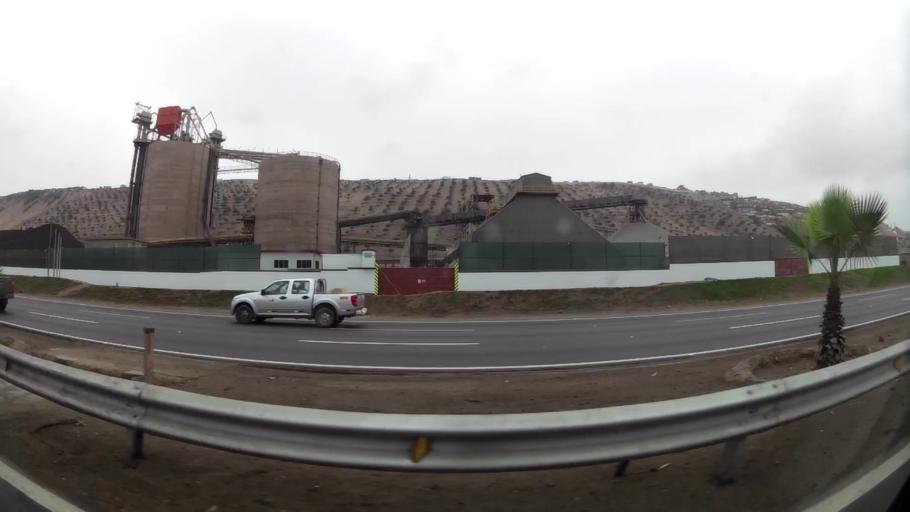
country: PE
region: Lima
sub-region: Lima
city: Surco
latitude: -12.2471
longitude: -76.9350
